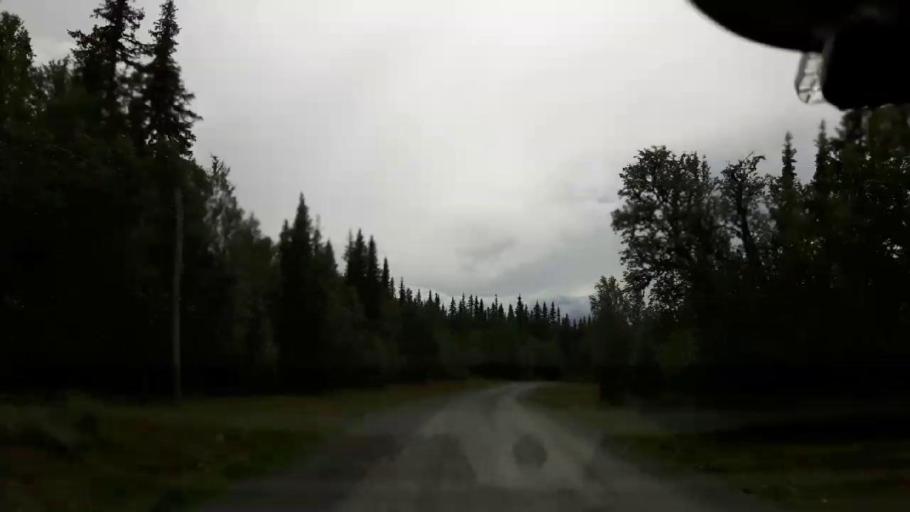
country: SE
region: Jaemtland
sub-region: Krokoms Kommun
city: Valla
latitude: 63.7569
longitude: 13.8376
